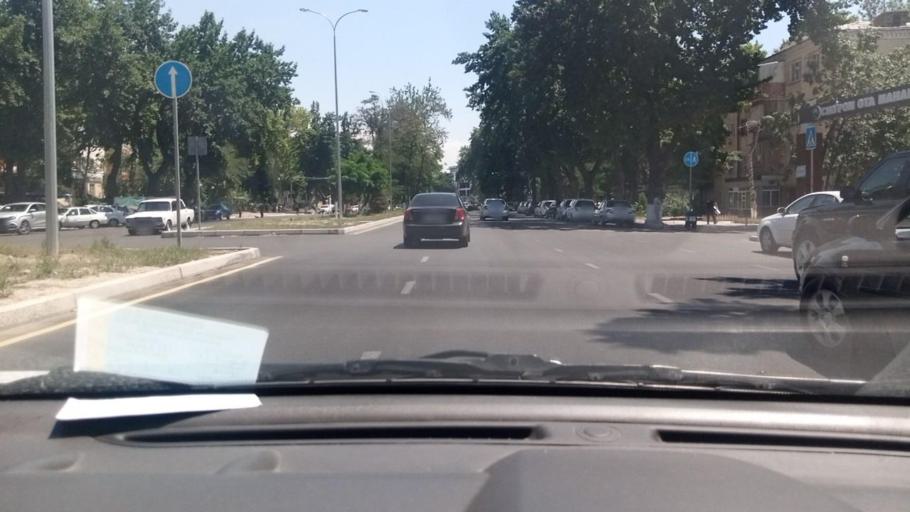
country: UZ
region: Toshkent Shahri
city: Tashkent
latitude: 41.2909
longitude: 69.2001
